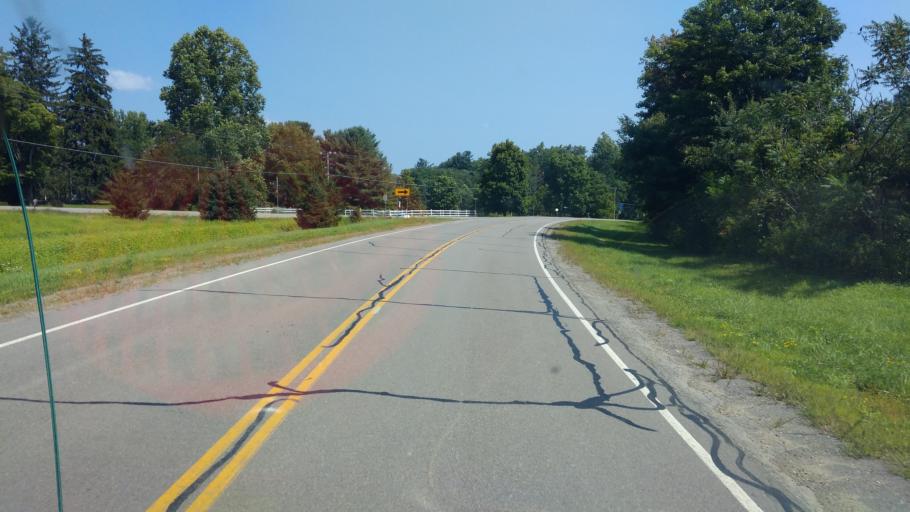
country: US
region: New York
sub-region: Allegany County
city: Belmont
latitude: 42.3070
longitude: -78.0460
